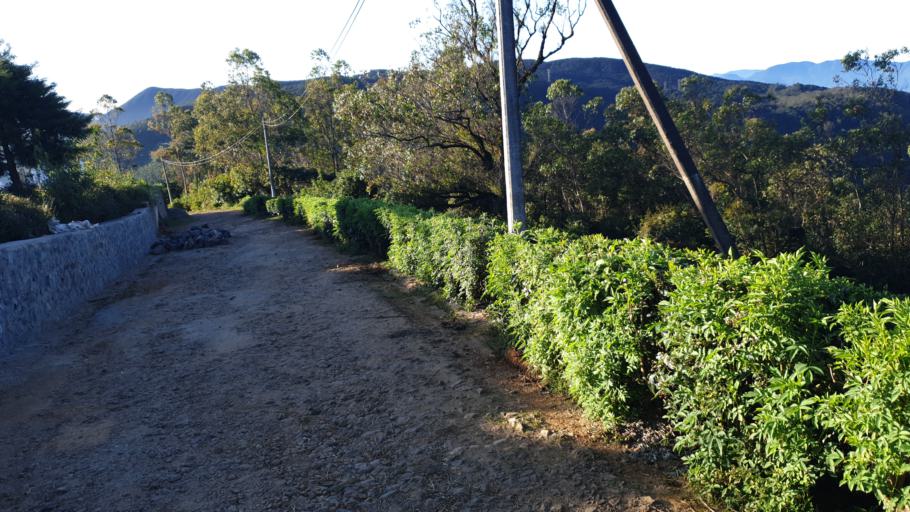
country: LK
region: Central
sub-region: Nuwara Eliya District
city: Nuwara Eliya
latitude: 6.9551
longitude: 80.7661
